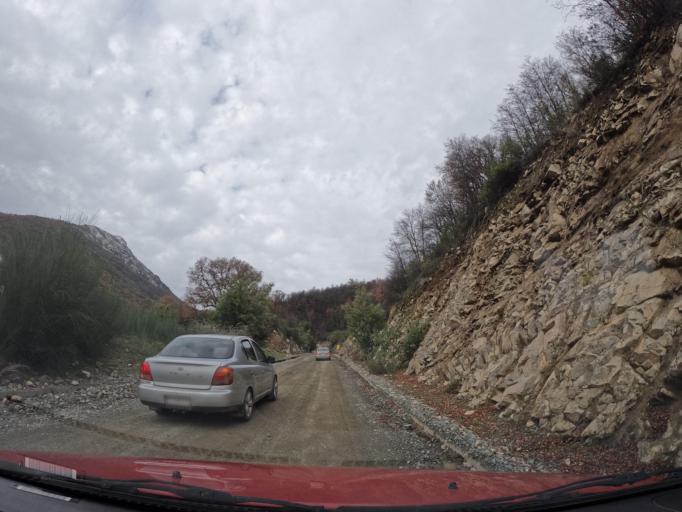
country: CL
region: Maule
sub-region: Provincia de Linares
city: Colbun
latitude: -35.8568
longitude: -71.1871
